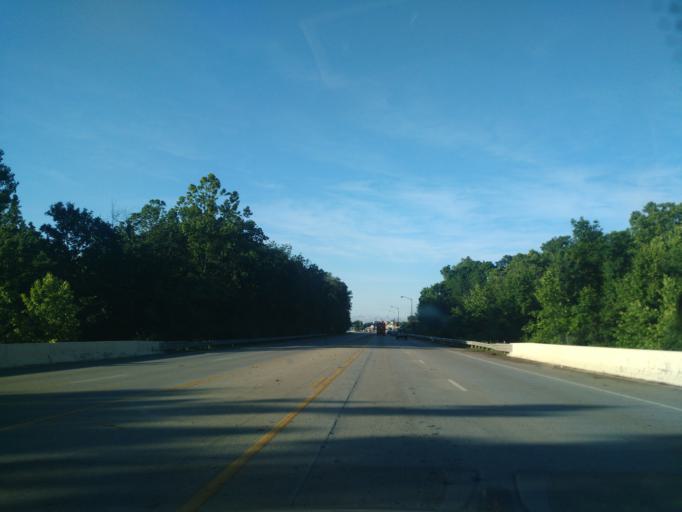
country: US
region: Ohio
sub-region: Pike County
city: Waverly
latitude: 39.1376
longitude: -82.9780
